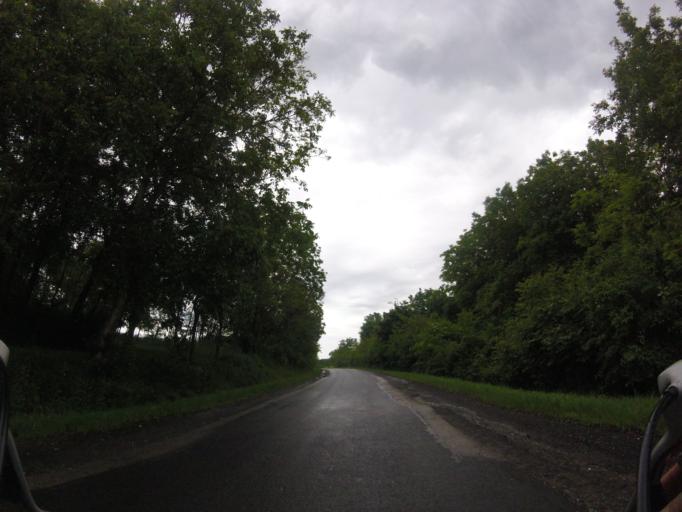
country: HU
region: Baranya
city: Pellerd
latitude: 45.9554
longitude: 18.2092
